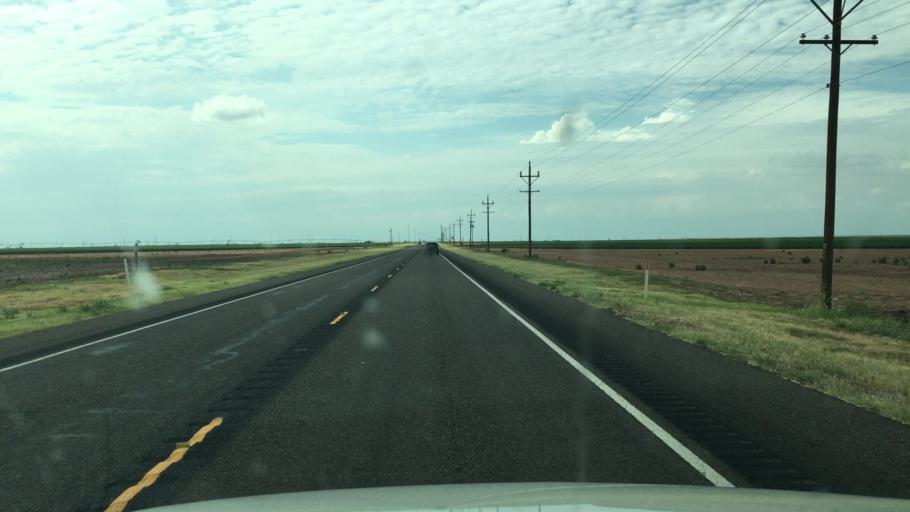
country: US
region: Texas
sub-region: Dawson County
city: Lamesa
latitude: 32.8838
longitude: -102.0836
